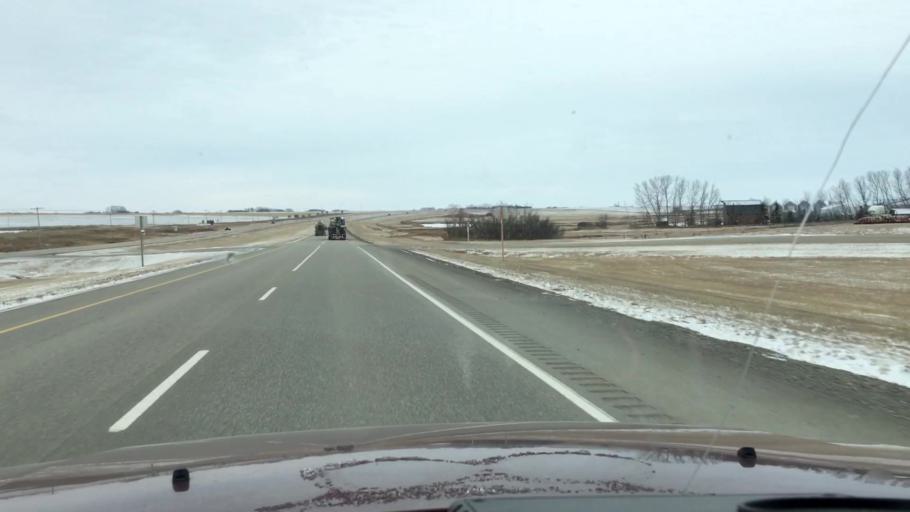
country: CA
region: Saskatchewan
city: Watrous
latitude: 51.2422
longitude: -105.9663
